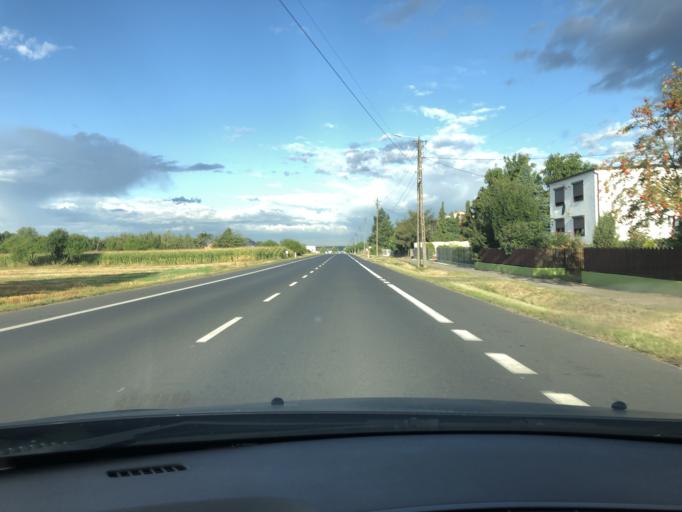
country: PL
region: Lodz Voivodeship
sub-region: Powiat wieruszowski
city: Galewice
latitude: 51.3034
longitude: 18.2783
